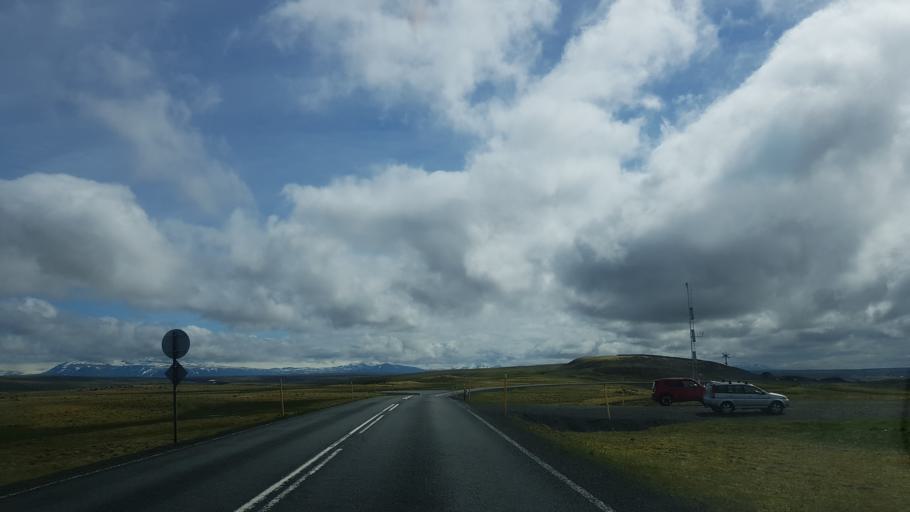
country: IS
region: West
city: Borgarnes
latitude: 64.9906
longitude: -21.0584
